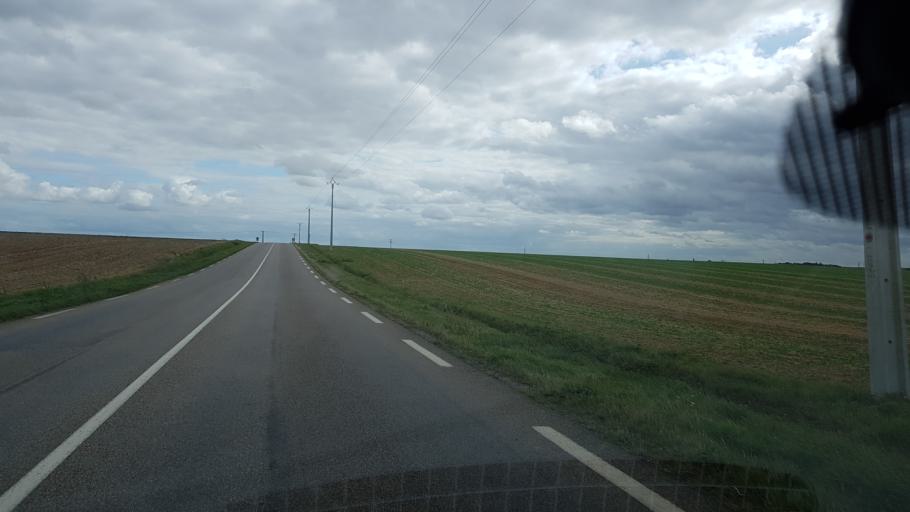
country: FR
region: Ile-de-France
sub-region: Departement de l'Essonne
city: Saclas
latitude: 48.3550
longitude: 2.1699
